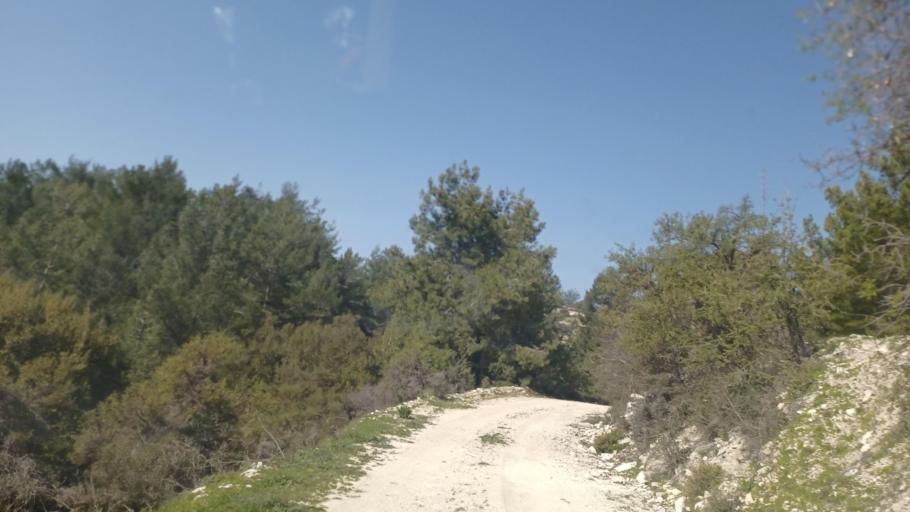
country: CY
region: Limassol
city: Pachna
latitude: 34.8835
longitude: 32.7168
